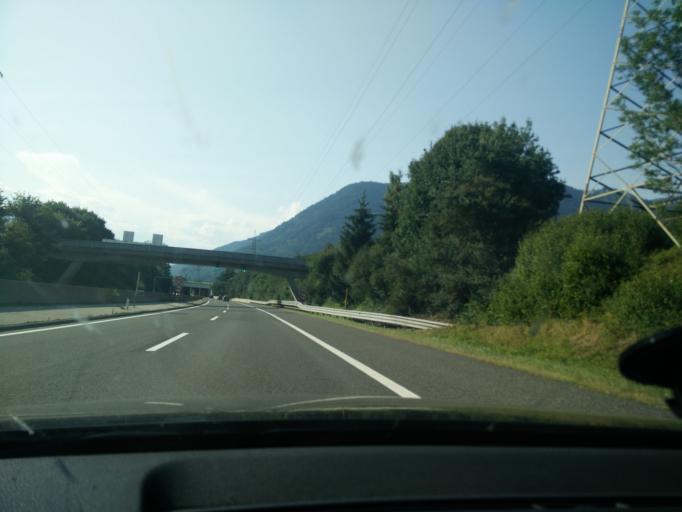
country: AT
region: Carinthia
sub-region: Politischer Bezirk Villach Land
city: Wernberg
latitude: 46.6359
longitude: 13.8936
